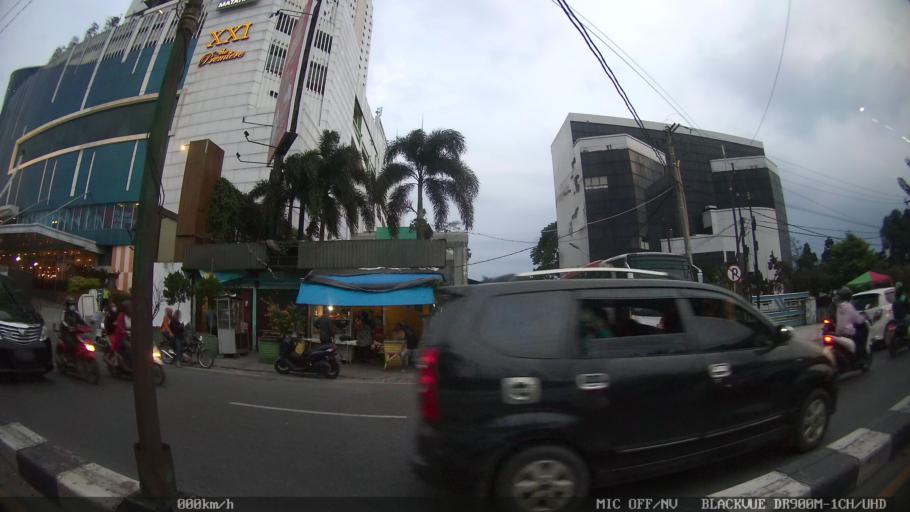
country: ID
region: North Sumatra
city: Sunggal
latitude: 3.5916
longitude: 98.6260
